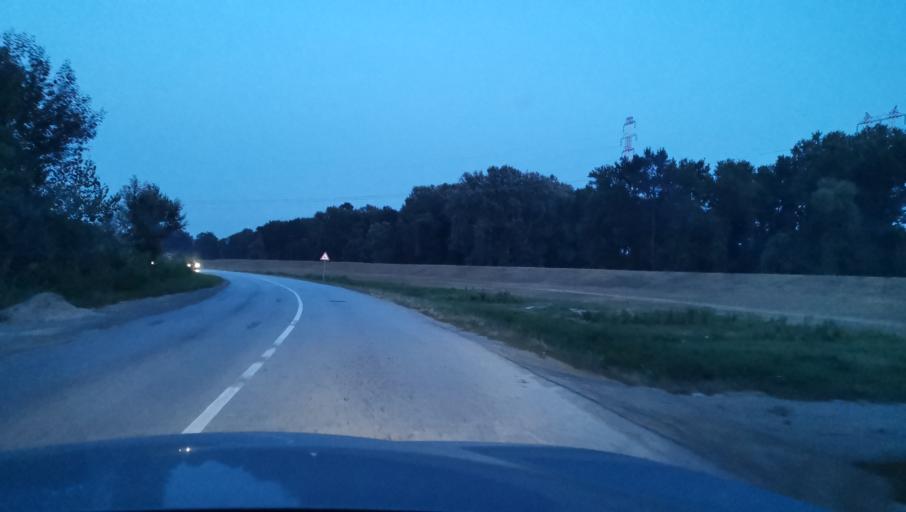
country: RS
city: Zvecka
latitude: 44.6771
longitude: 20.1692
